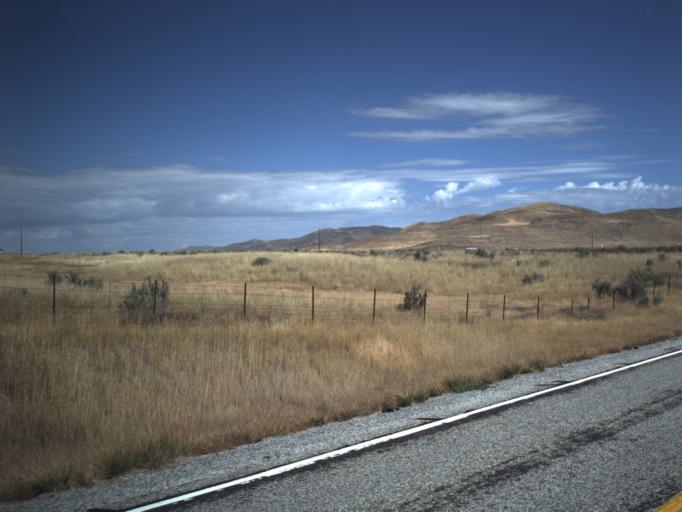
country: US
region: Utah
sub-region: Box Elder County
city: Garland
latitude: 41.7924
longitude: -112.4207
